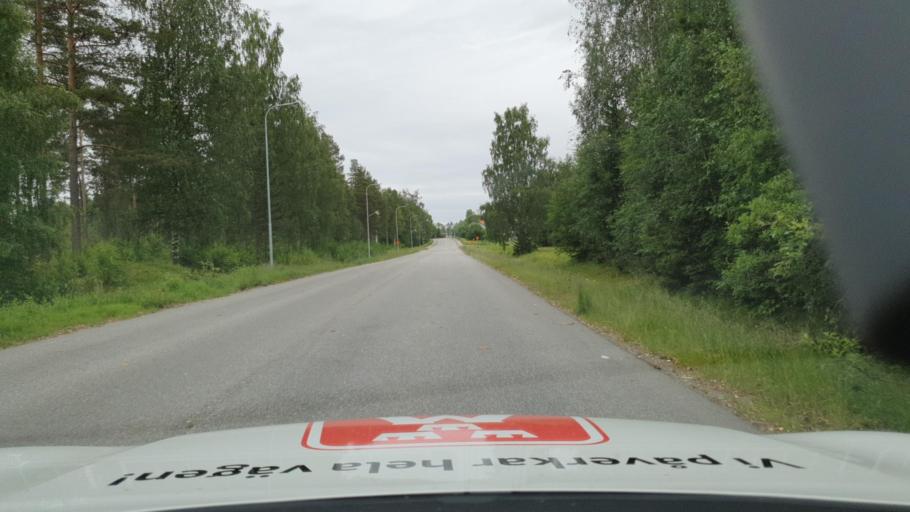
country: SE
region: Vaesterbotten
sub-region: Nordmalings Kommun
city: Nordmaling
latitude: 63.5454
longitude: 19.4375
